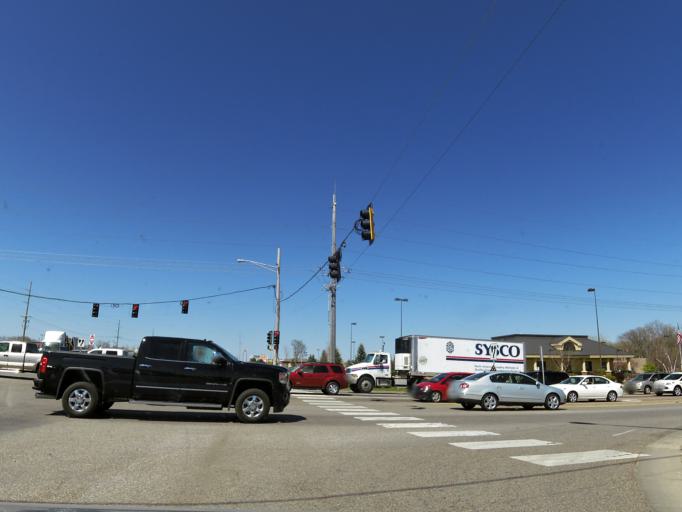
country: US
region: Minnesota
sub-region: Scott County
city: Prior Lake
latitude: 44.7461
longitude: -93.3795
